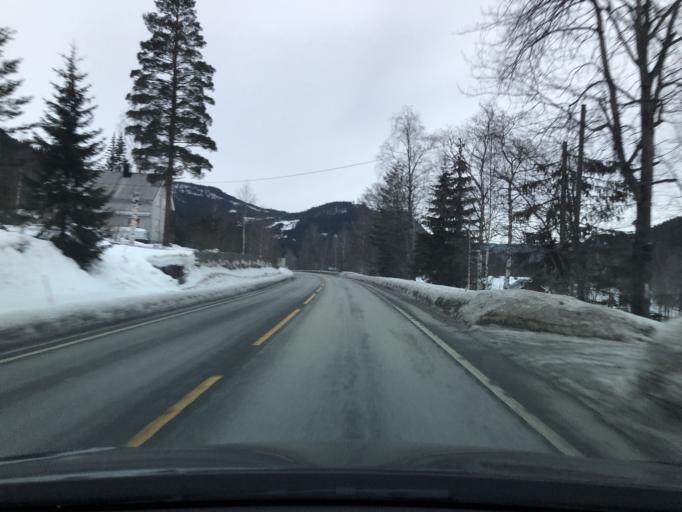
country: NO
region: Oppland
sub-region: Etnedal
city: Bruflat
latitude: 60.7014
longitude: 9.7180
